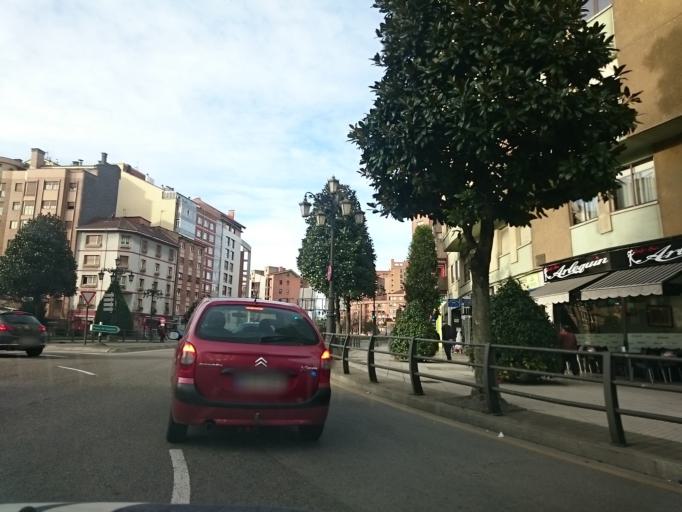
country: ES
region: Asturias
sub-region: Province of Asturias
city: Oviedo
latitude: 43.3552
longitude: -5.8475
